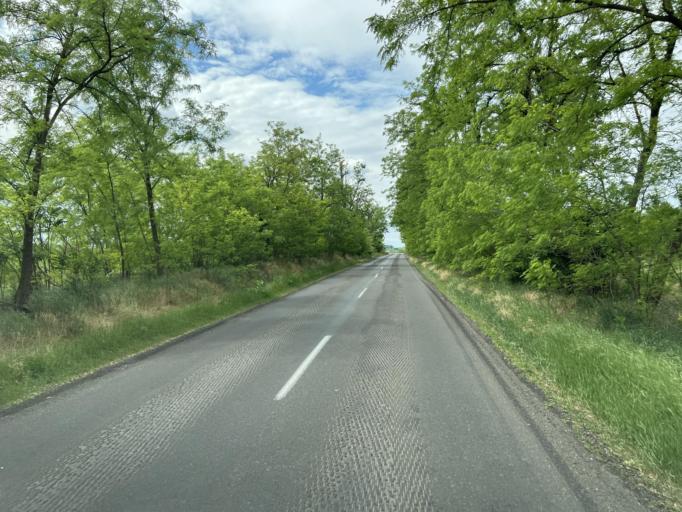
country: HU
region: Pest
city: Szentmartonkata
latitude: 47.4706
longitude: 19.7125
